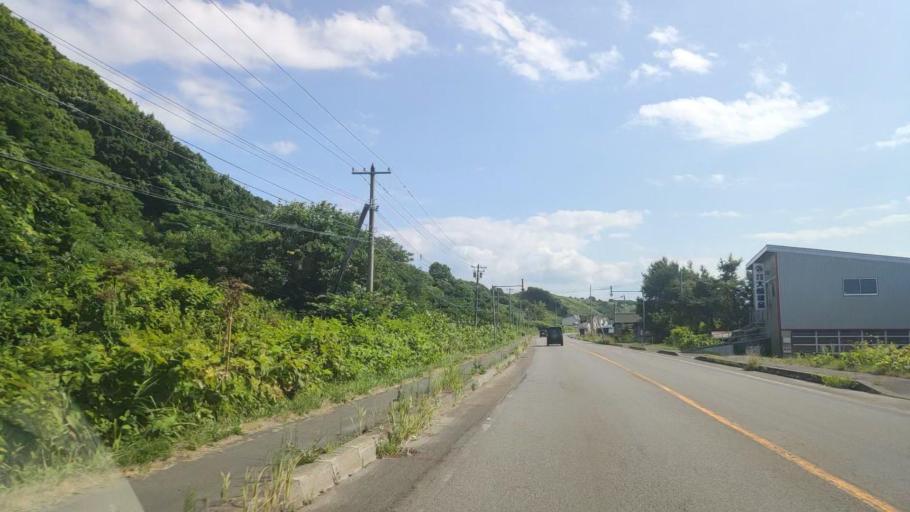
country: JP
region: Hokkaido
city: Rumoi
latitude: 43.9729
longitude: 141.6466
